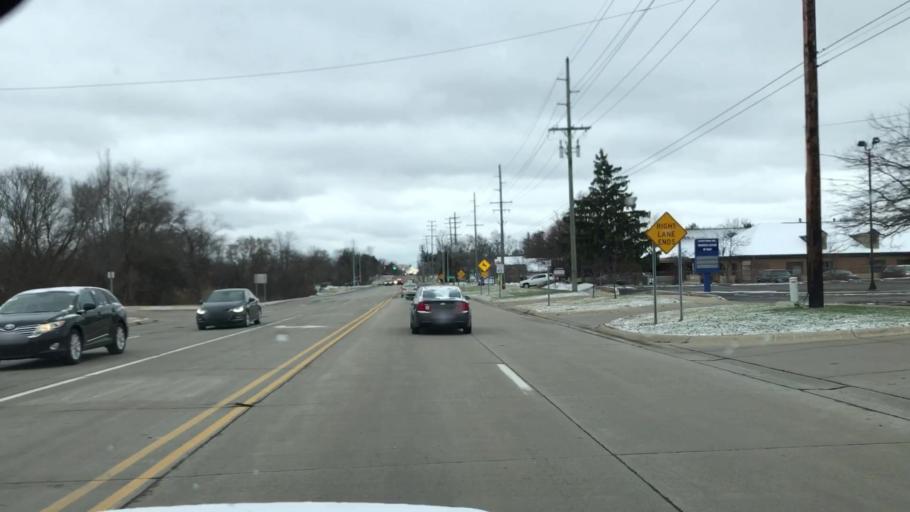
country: US
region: Michigan
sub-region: Oakland County
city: Novi
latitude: 42.4663
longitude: -83.4747
